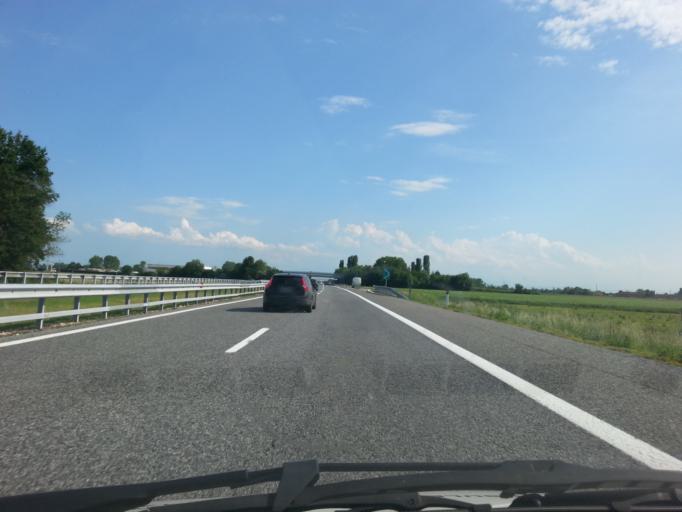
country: IT
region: Piedmont
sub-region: Provincia di Cuneo
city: Caramagna Piemonte
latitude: 44.7463
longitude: 7.7509
